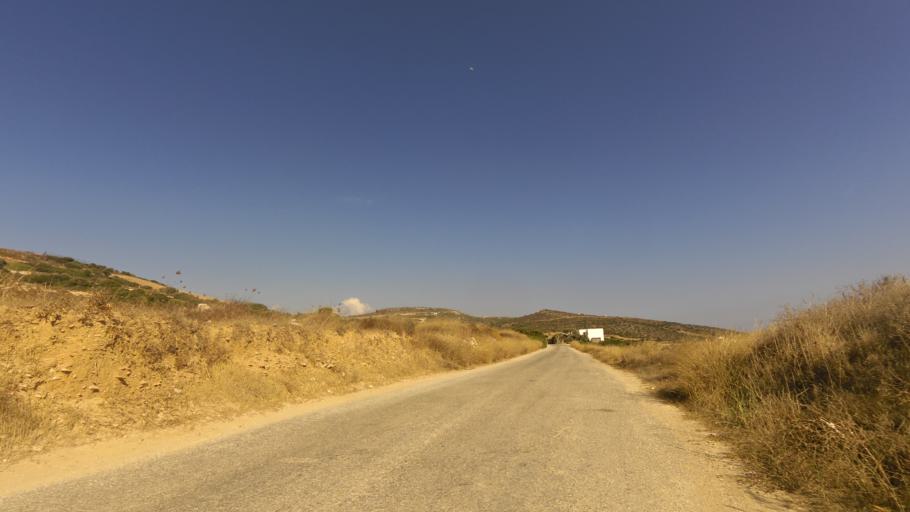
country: GR
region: South Aegean
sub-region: Nomos Kykladon
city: Antiparos
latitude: 37.0180
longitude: 25.0559
